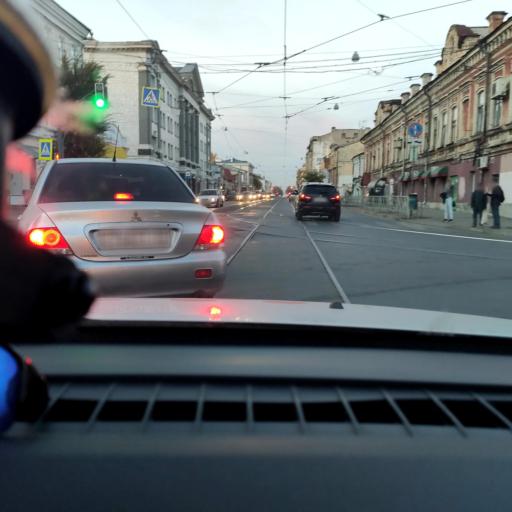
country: RU
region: Samara
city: Rozhdestveno
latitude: 53.1850
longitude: 50.0897
